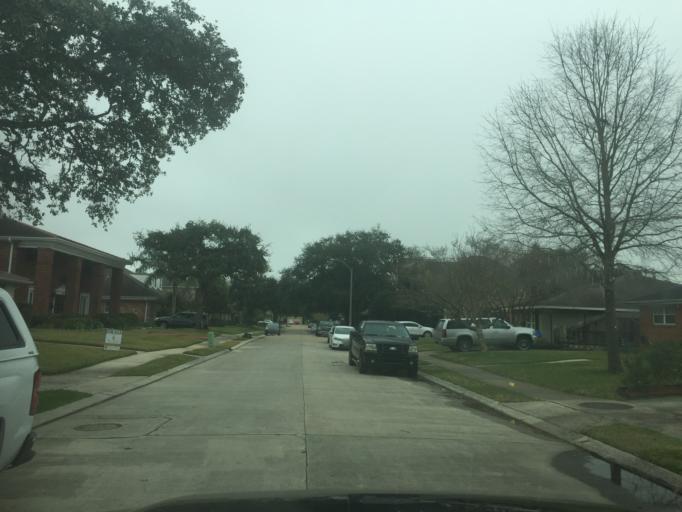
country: US
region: Louisiana
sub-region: Jefferson Parish
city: Metairie
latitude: 30.0201
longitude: -90.1021
